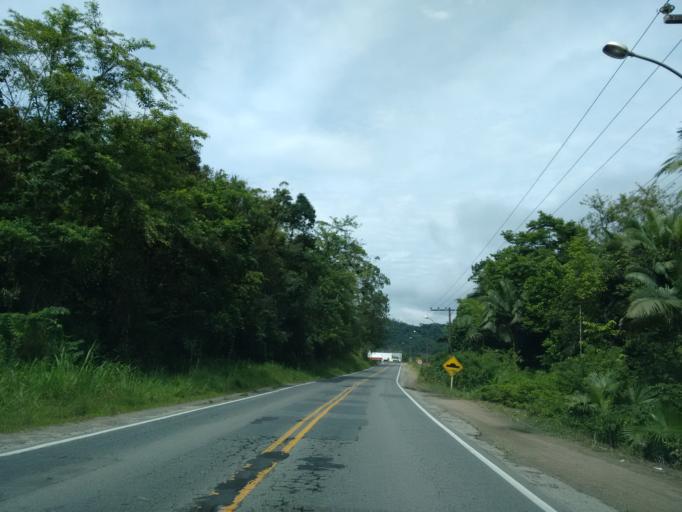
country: BR
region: Santa Catarina
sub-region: Pomerode
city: Pomerode
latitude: -26.6897
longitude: -49.1542
